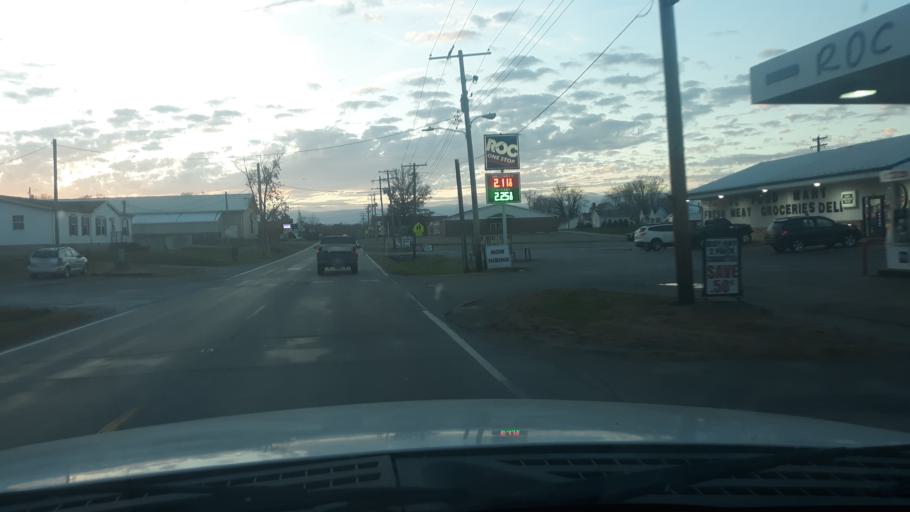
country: US
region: Illinois
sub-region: Saline County
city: Harrisburg
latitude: 37.8408
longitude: -88.6091
